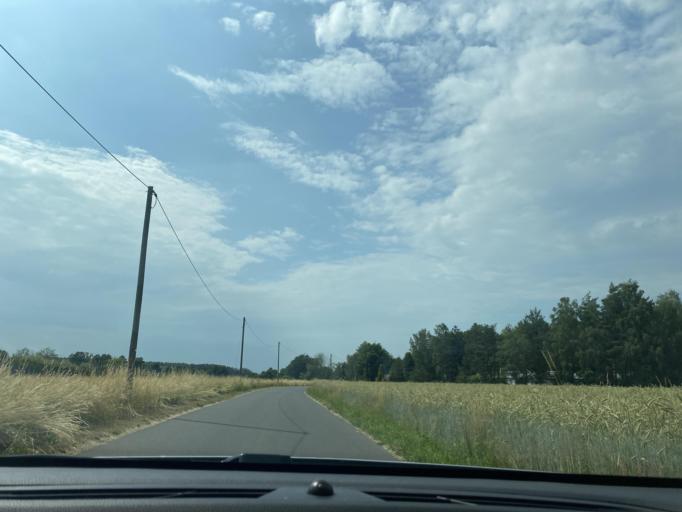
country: DE
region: Saxony
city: Quitzdorf
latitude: 51.2664
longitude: 14.7916
